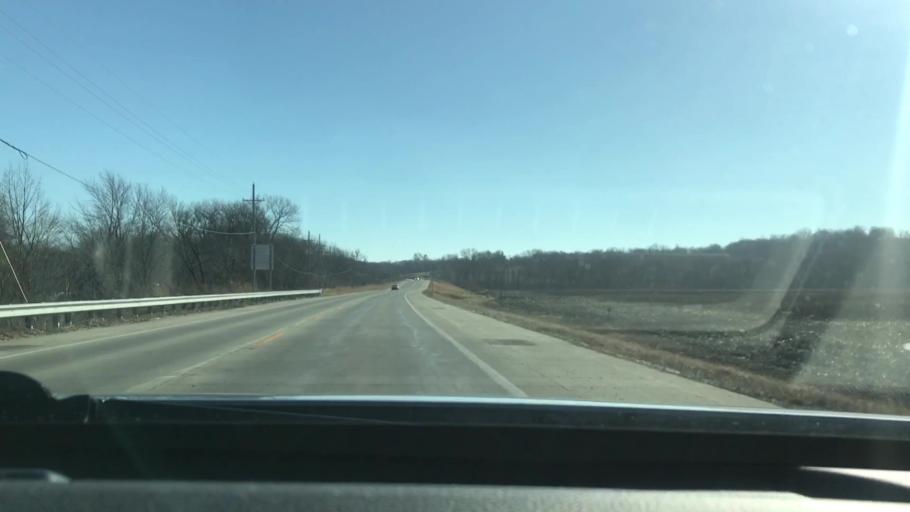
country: US
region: Missouri
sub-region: Platte County
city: Platte City
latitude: 39.3740
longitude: -94.7912
